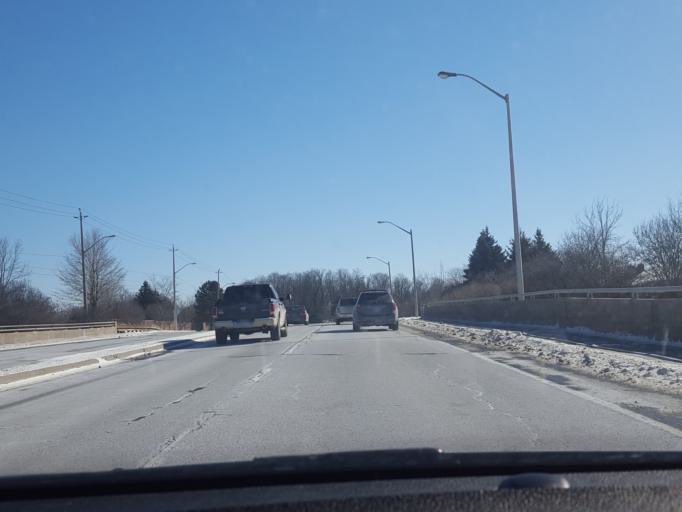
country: CA
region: Ontario
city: Kitchener
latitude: 43.4409
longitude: -80.5393
